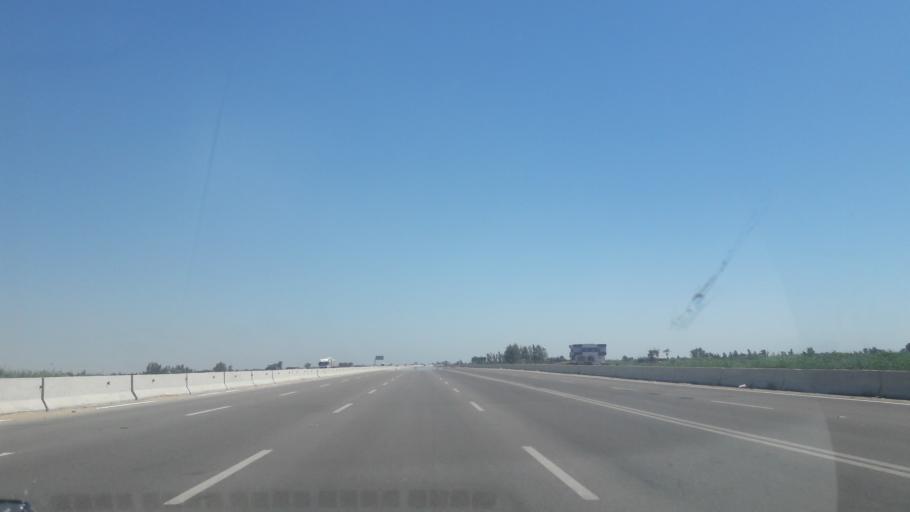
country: EG
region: Muhafazat Bur Sa`id
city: Port Said
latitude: 31.0802
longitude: 32.2341
